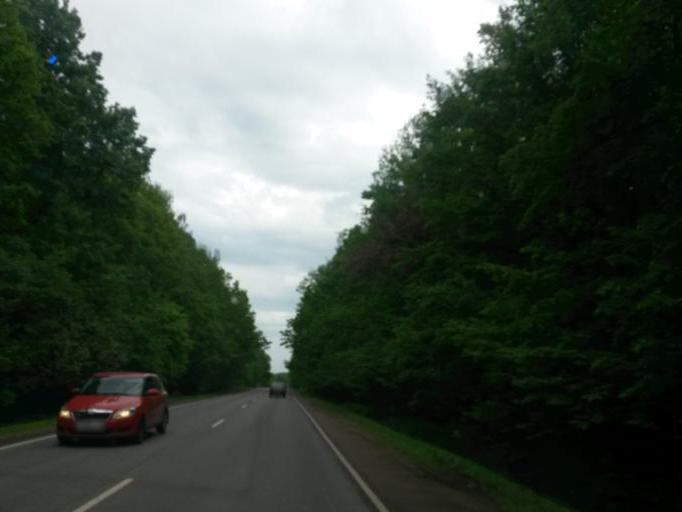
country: RU
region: Moskovskaya
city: Melikhovo
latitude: 55.1875
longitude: 37.7076
